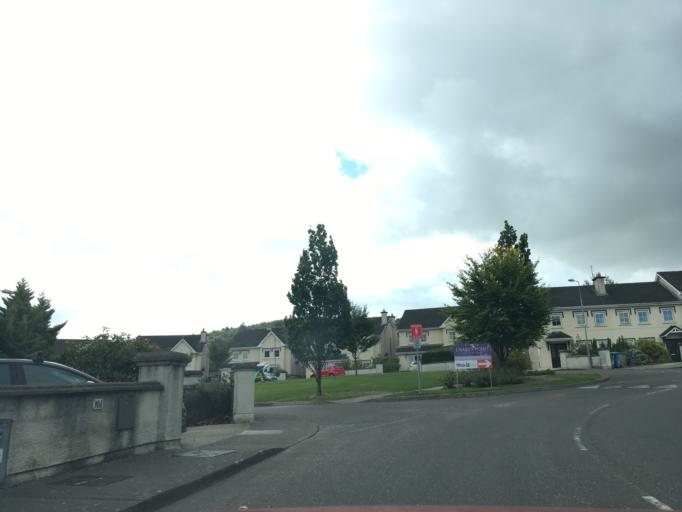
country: IE
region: Munster
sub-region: County Cork
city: Crosshaven
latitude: 51.7997
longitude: -8.2936
